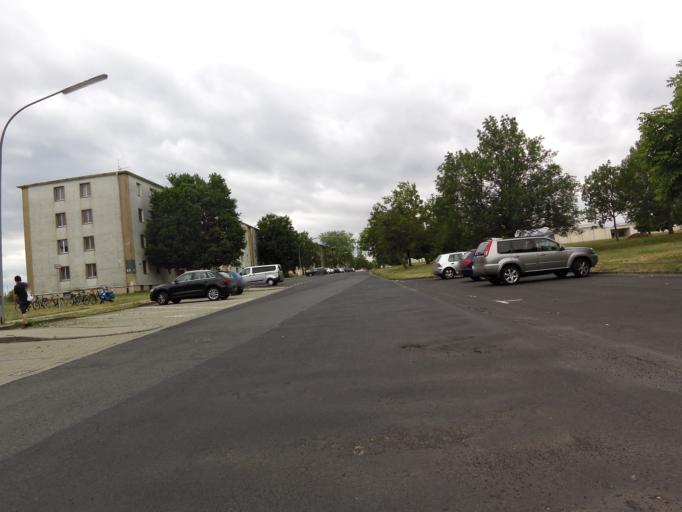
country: DE
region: Bavaria
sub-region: Regierungsbezirk Unterfranken
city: Gerbrunn
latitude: 49.7882
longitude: 9.9767
